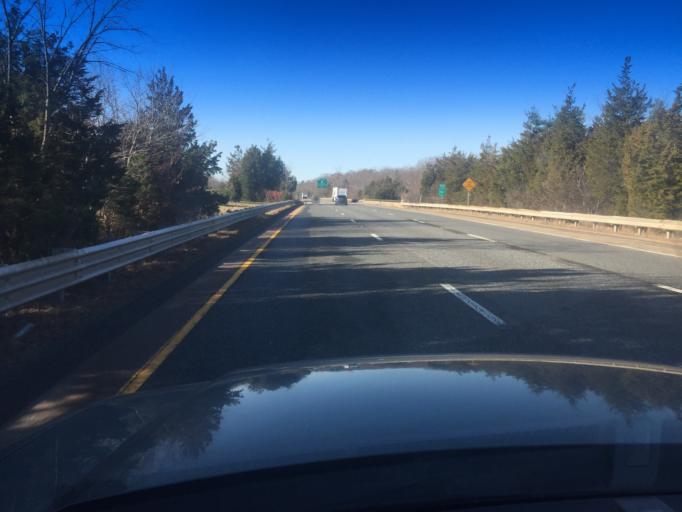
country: US
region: Massachusetts
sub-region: Bristol County
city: Attleboro
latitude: 41.9529
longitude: -71.3237
